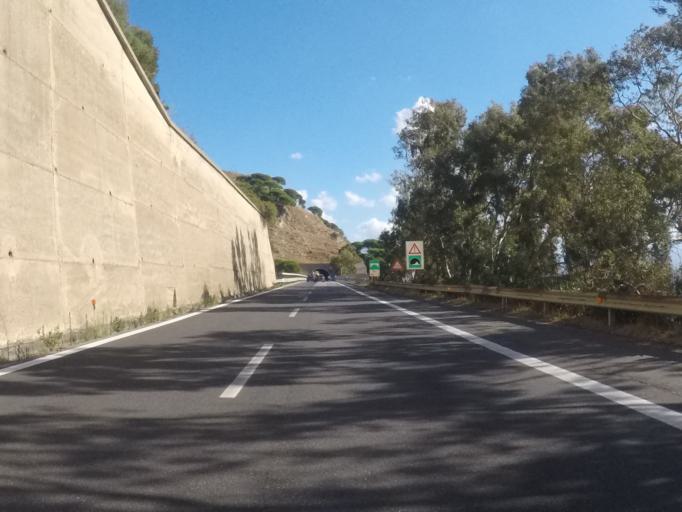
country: IT
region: Sicily
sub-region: Messina
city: Scaletta Zanclea
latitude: 38.0698
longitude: 15.4860
